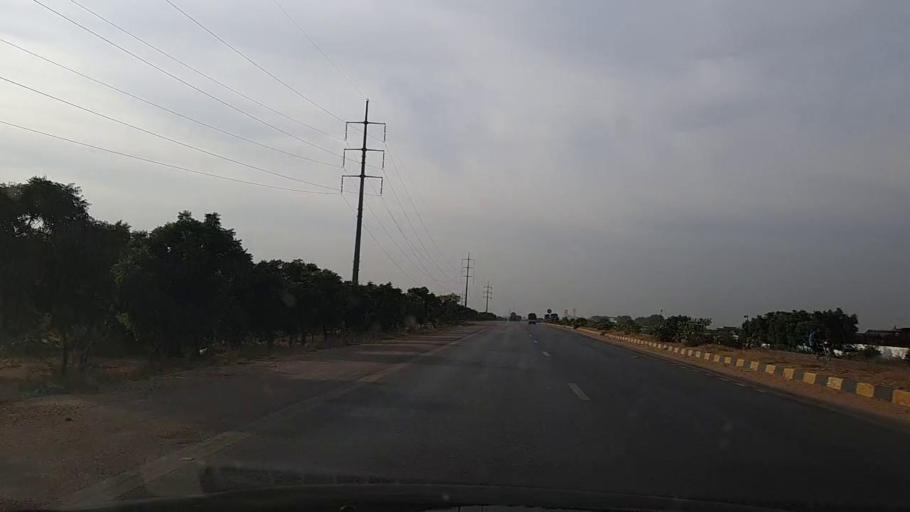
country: PK
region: Sindh
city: Gharo
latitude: 24.8338
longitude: 67.4584
